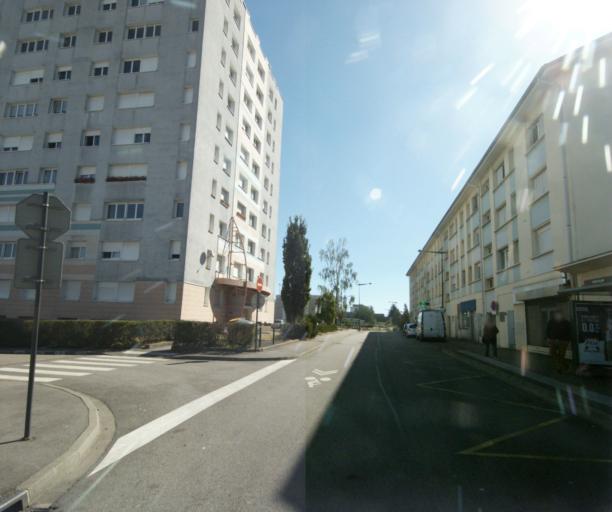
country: FR
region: Lorraine
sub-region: Departement des Vosges
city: Epinal
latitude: 48.1835
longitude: 6.4548
